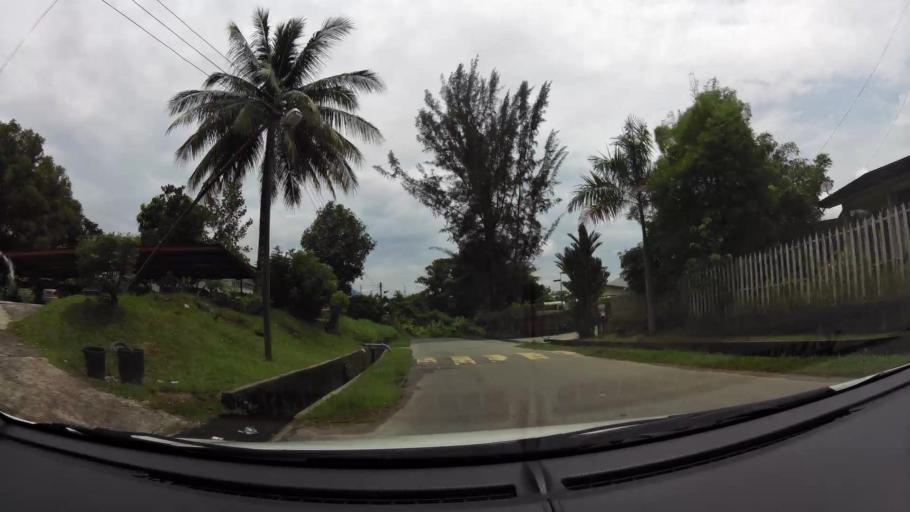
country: BN
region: Brunei and Muara
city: Bandar Seri Begawan
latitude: 4.8906
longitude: 114.9246
